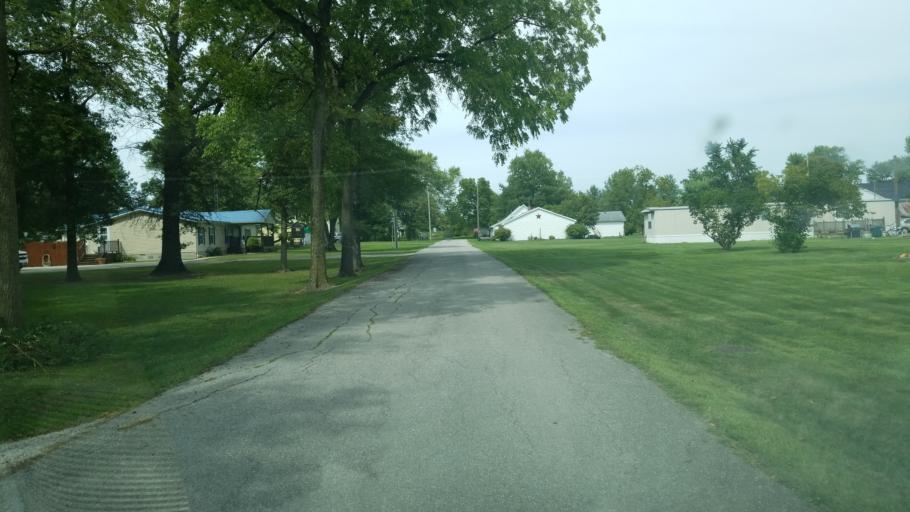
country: US
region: Ohio
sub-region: Union County
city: Richwood
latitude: 40.5839
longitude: -83.3184
